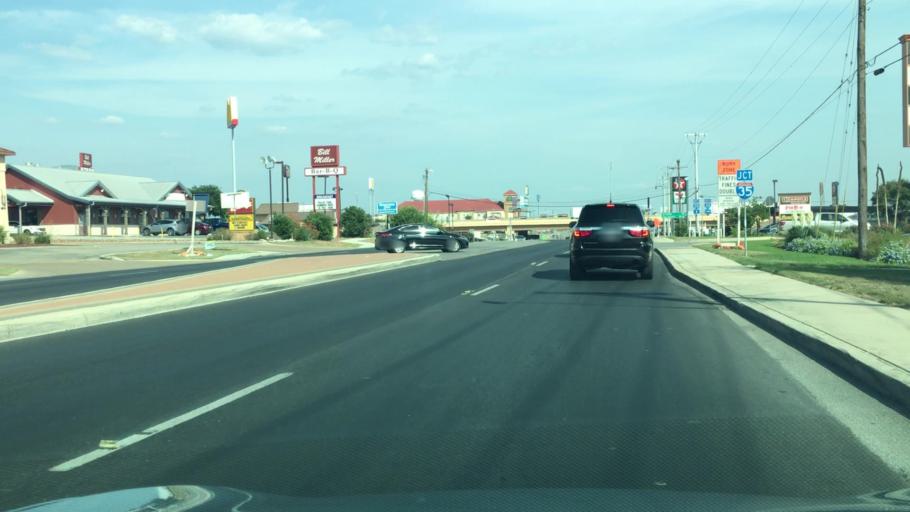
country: US
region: Texas
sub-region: Comal County
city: New Braunfels
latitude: 29.7018
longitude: -98.0958
